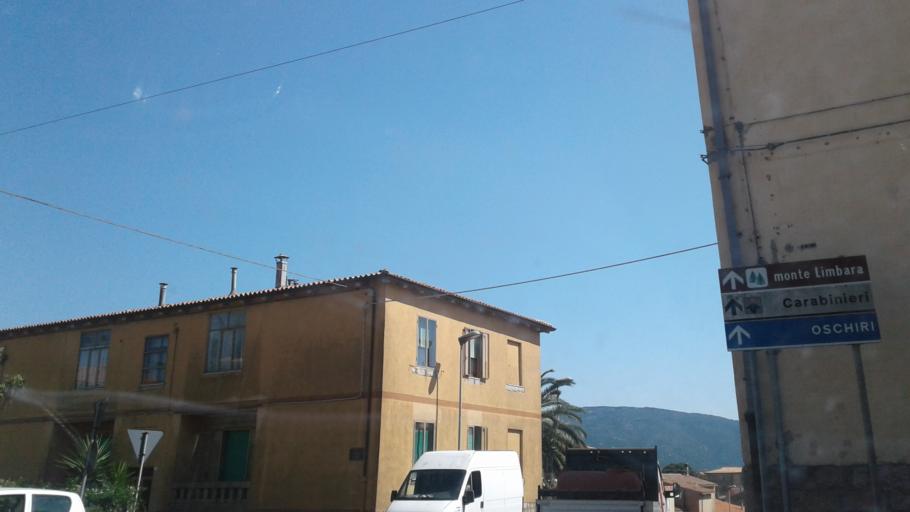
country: IT
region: Sardinia
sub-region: Provincia di Olbia-Tempio
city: Tempio Pausania
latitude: 40.9013
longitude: 9.1088
